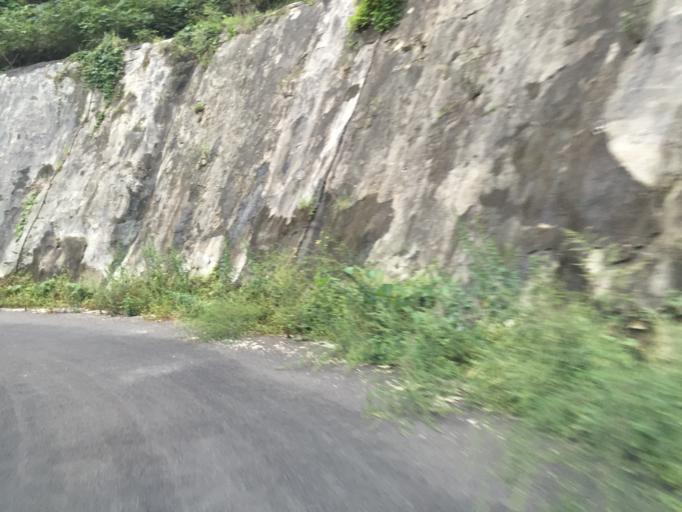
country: JP
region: Fukushima
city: Fukushima-shi
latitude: 37.7532
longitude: 140.5024
